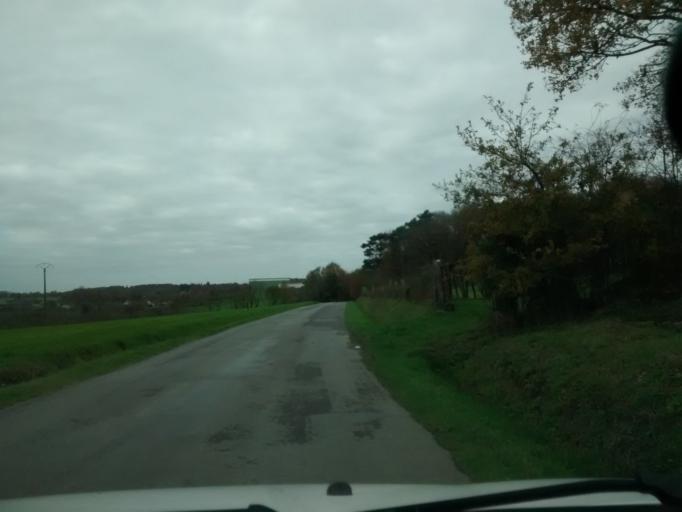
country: FR
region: Brittany
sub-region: Departement d'Ille-et-Vilaine
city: Erbree
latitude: 48.0986
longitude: -1.1501
